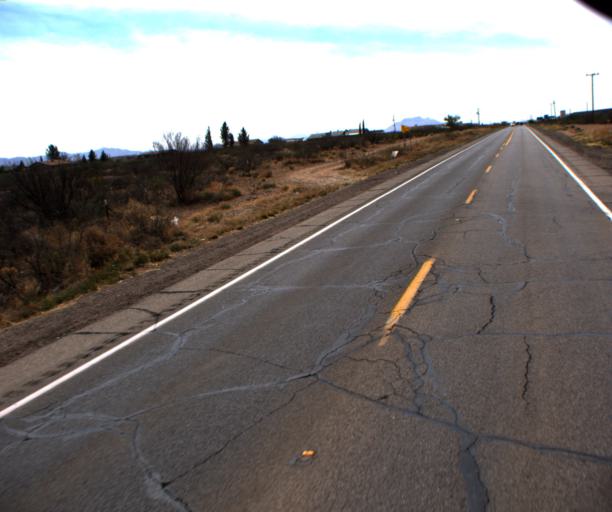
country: US
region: Arizona
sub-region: Cochise County
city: Pirtleville
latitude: 31.3607
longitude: -109.5794
